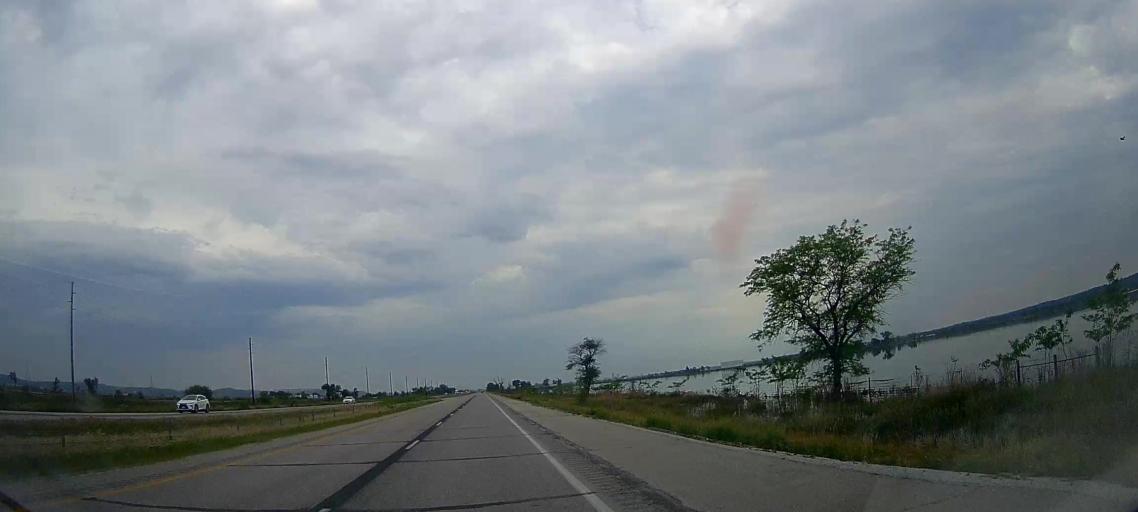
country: US
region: Iowa
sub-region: Pottawattamie County
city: Carter Lake
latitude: 41.4074
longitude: -95.8999
